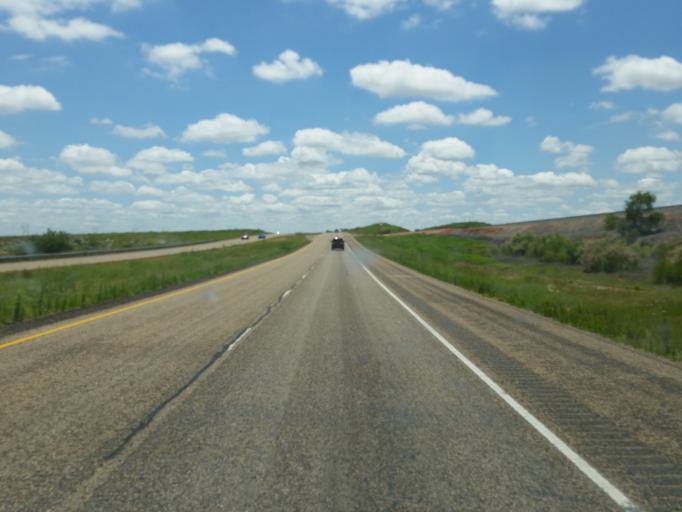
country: US
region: Texas
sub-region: Garza County
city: Post
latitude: 33.1120
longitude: -101.2721
